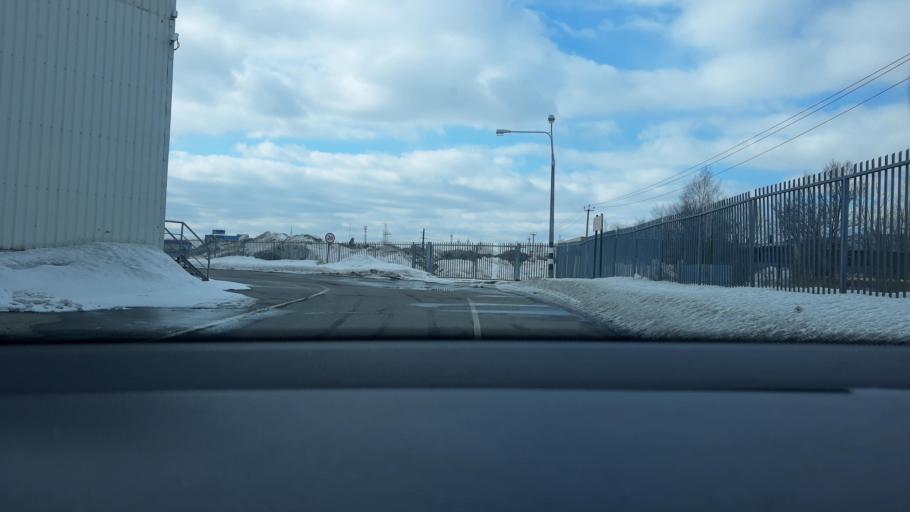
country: RU
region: Moskovskaya
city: Lesnyye Polyany
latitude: 55.9814
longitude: 37.8766
